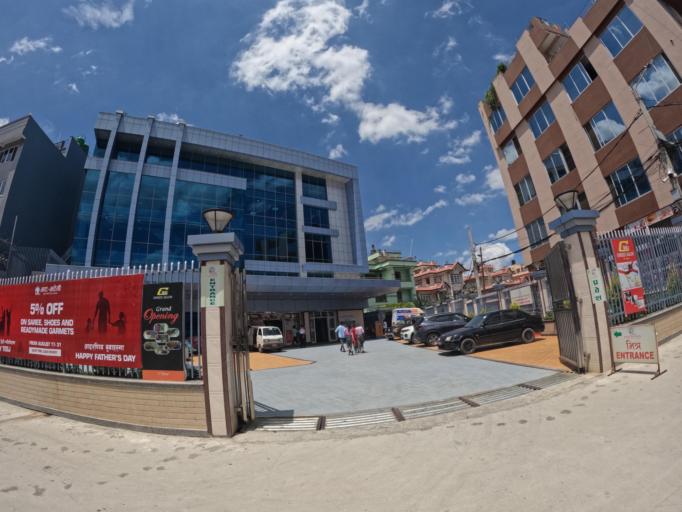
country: NP
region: Central Region
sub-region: Bagmati Zone
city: Kathmandu
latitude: 27.7494
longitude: 85.3250
